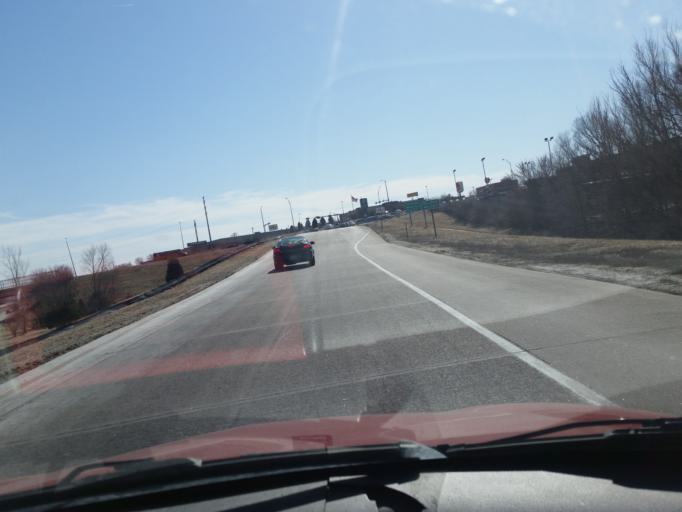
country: US
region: Nebraska
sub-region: Sarpy County
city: Offutt Air Force Base
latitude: 41.1610
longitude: -95.9395
